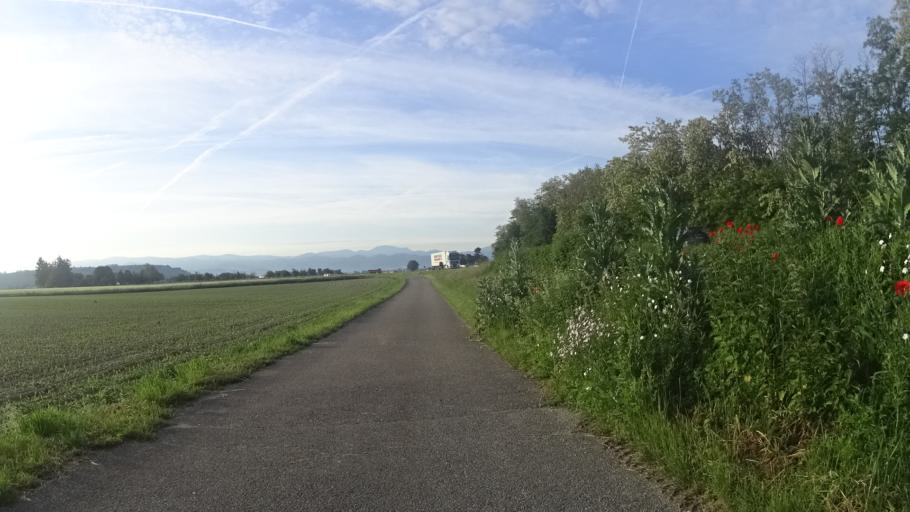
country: DE
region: Baden-Wuerttemberg
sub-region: Freiburg Region
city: Hartheim
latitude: 47.9853
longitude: 7.6409
